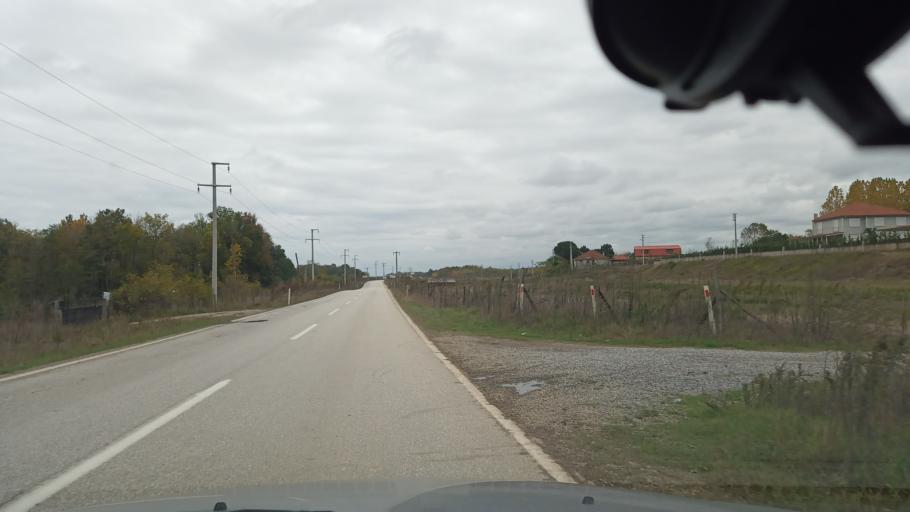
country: TR
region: Sakarya
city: Karasu
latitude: 41.1233
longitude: 30.5638
